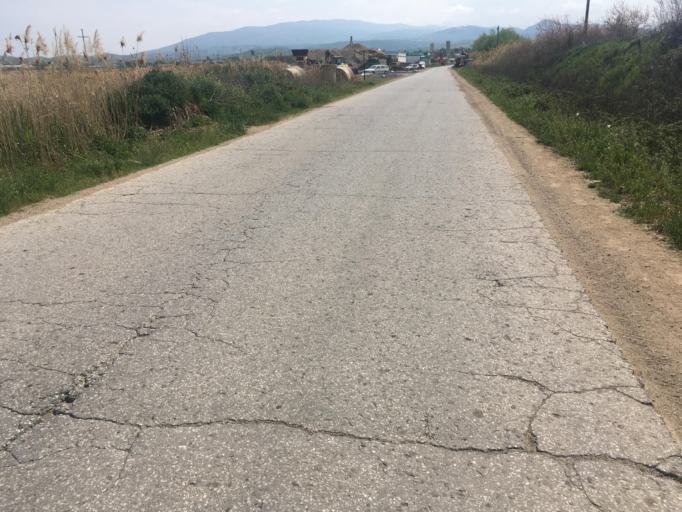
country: MK
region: Karbinci
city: Karbinci
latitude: 41.8007
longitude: 22.2151
